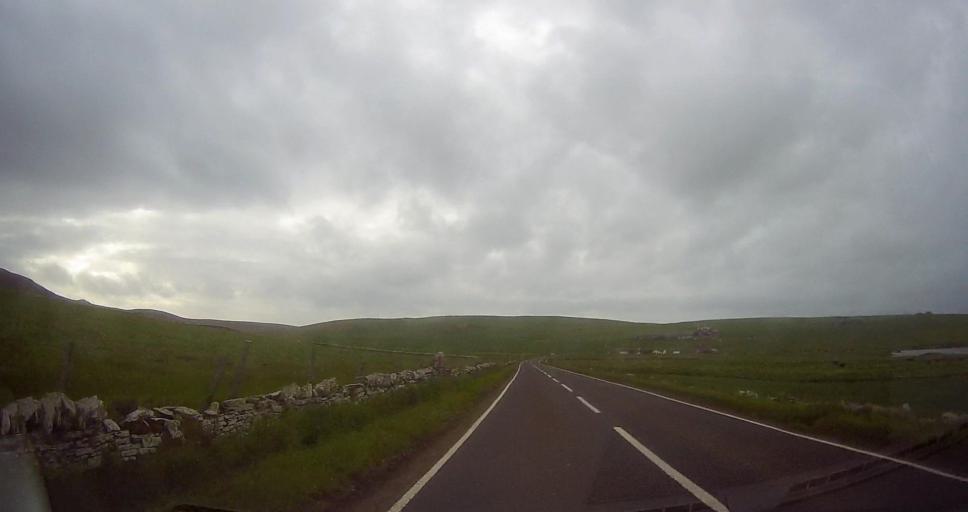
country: GB
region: Scotland
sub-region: Orkney Islands
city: Stromness
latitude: 59.0115
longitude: -3.2972
